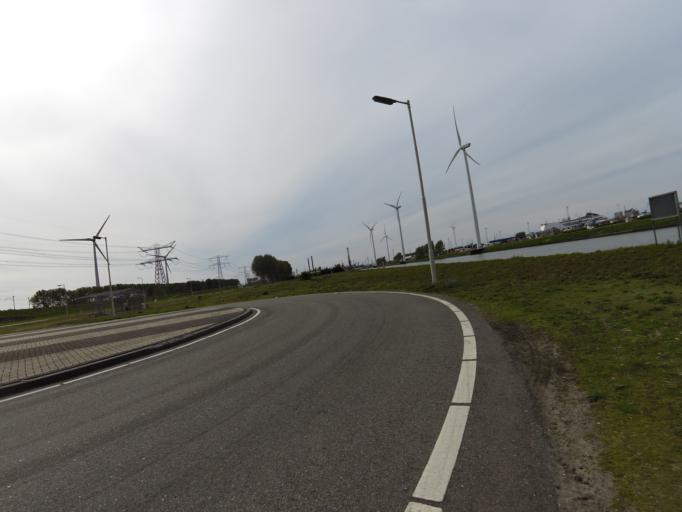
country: NL
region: South Holland
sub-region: Gemeente Rotterdam
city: Hoek van Holland
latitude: 51.9360
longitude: 4.1379
